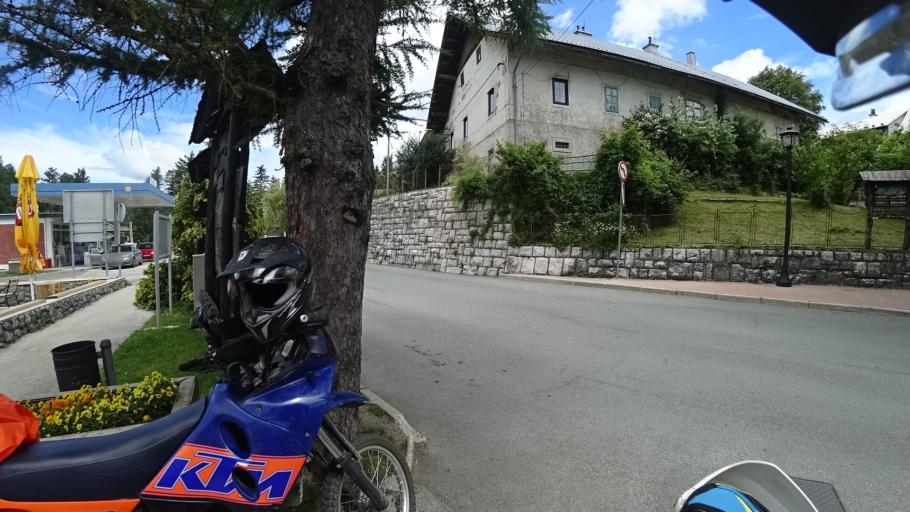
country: HR
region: Primorsko-Goranska
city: Hreljin
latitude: 45.3048
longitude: 14.7135
